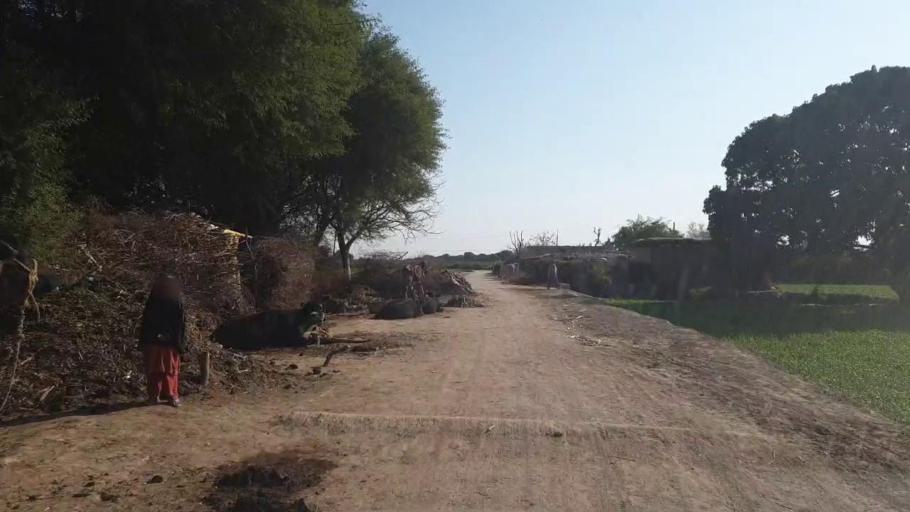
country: PK
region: Sindh
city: Tando Allahyar
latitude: 25.4052
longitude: 68.6680
